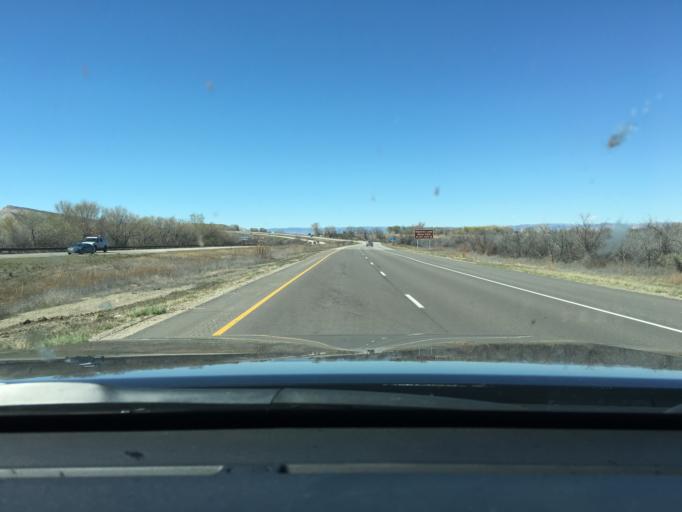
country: US
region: Colorado
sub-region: Mesa County
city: Loma
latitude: 39.1717
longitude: -108.7956
